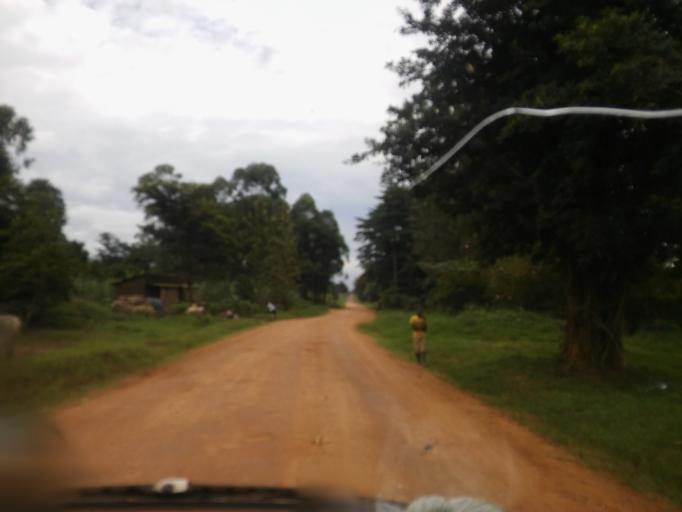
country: UG
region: Eastern Region
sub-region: Bududa District
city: Bududa
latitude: 0.9449
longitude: 34.2321
